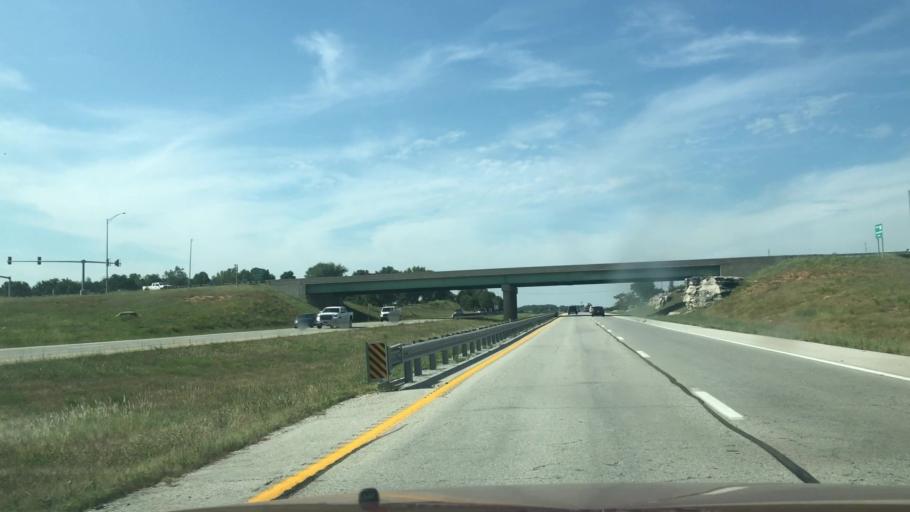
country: US
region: Missouri
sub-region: Christian County
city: Ozark
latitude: 37.0036
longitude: -93.2297
